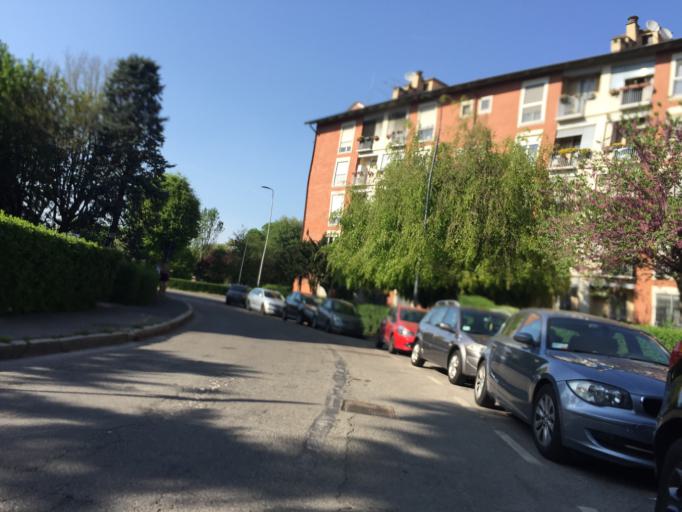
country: IT
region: Lombardy
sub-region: Citta metropolitana di Milano
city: Linate
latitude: 45.4598
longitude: 9.2469
